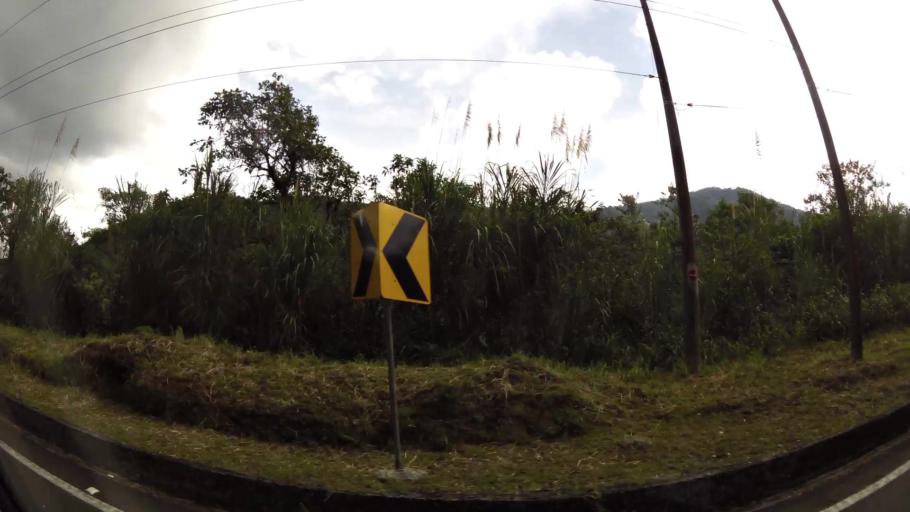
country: EC
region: Pastaza
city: Puyo
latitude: -1.4510
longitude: -78.1513
